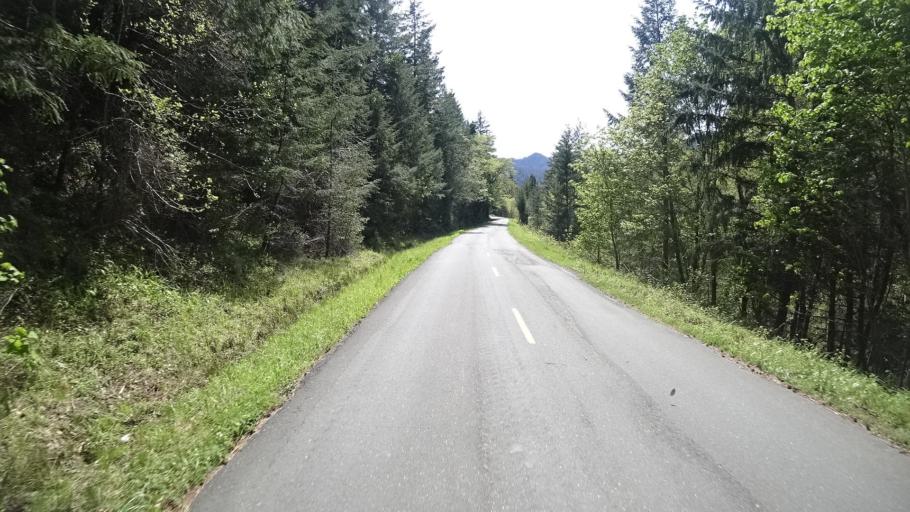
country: US
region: California
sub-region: Humboldt County
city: Redway
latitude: 40.3870
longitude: -123.7405
